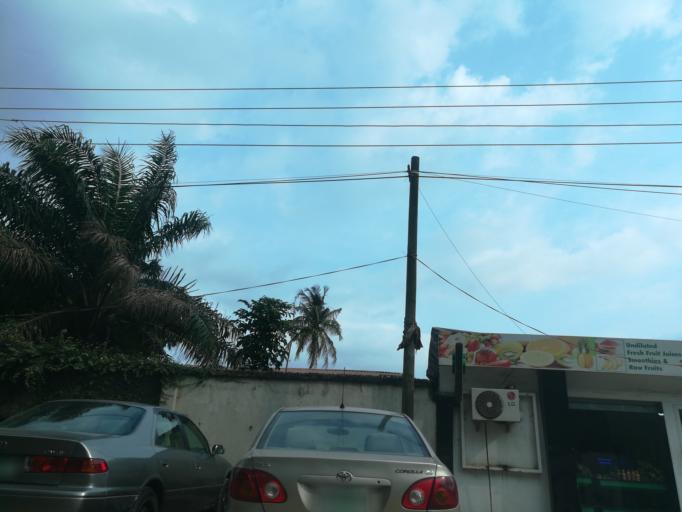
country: NG
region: Lagos
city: Oshodi
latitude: 6.5738
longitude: 3.3588
